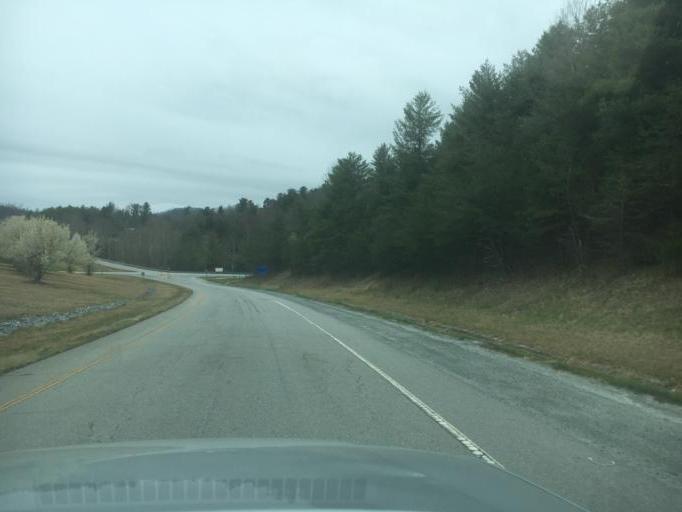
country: US
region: North Carolina
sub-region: Henderson County
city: Flat Rock
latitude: 35.2174
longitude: -82.4451
